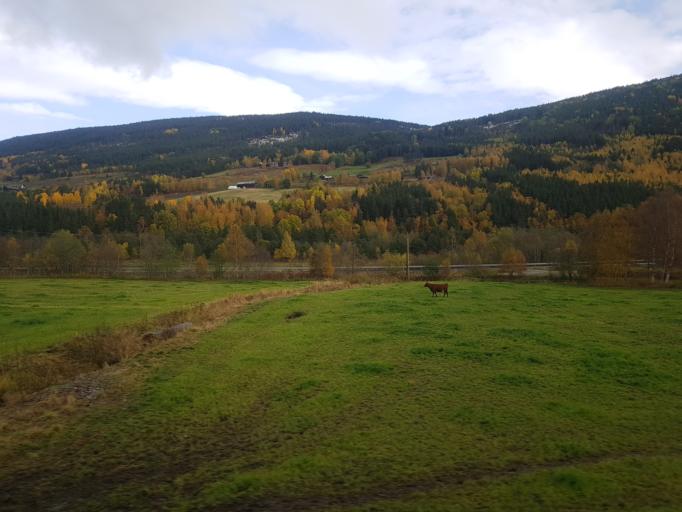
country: NO
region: Oppland
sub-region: Dovre
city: Dovre
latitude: 61.9874
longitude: 9.2413
